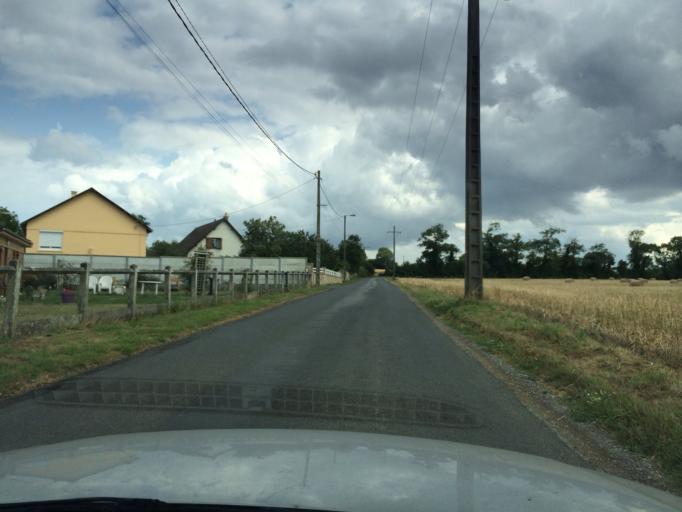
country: FR
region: Lower Normandy
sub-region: Departement du Calvados
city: Saint-Vigor-le-Grand
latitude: 49.3002
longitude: -0.6918
